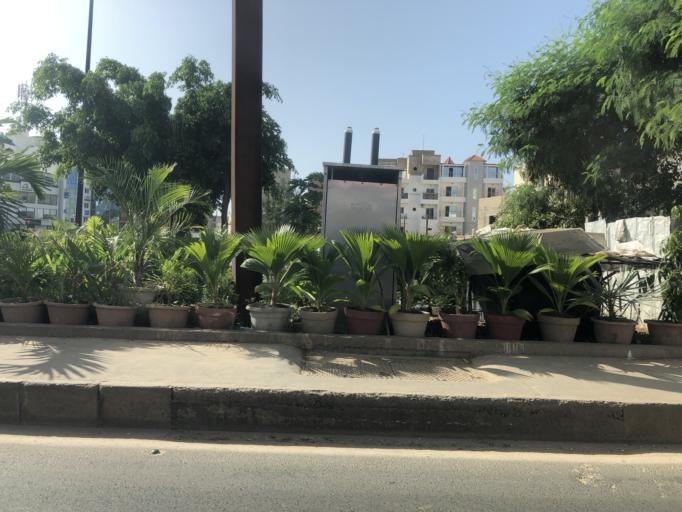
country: SN
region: Dakar
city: Mermoz Boabab
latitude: 14.7445
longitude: -17.5112
